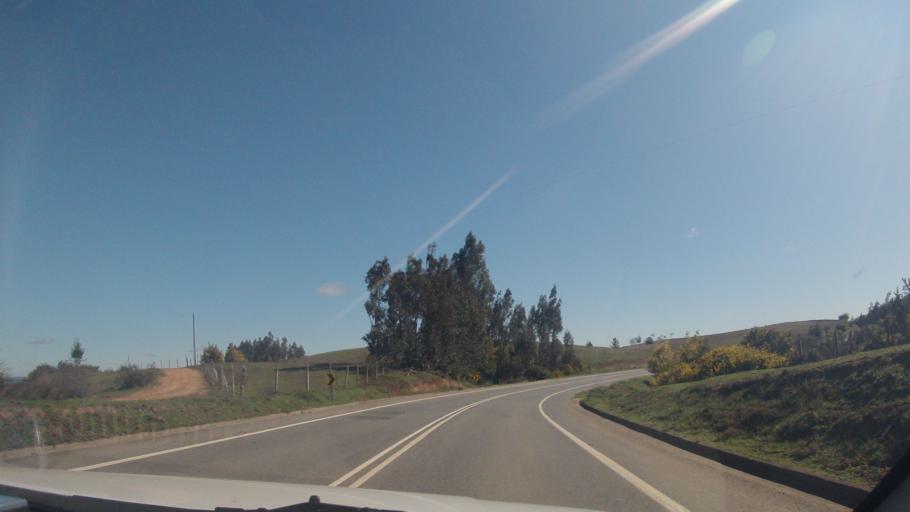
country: CL
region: Araucania
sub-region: Provincia de Malleco
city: Traiguen
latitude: -38.1742
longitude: -72.8453
